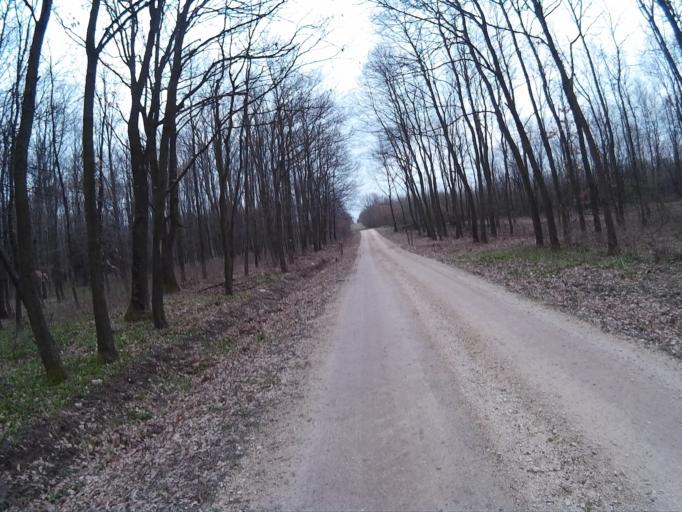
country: HU
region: Veszprem
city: Zirc
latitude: 47.1868
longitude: 17.9083
